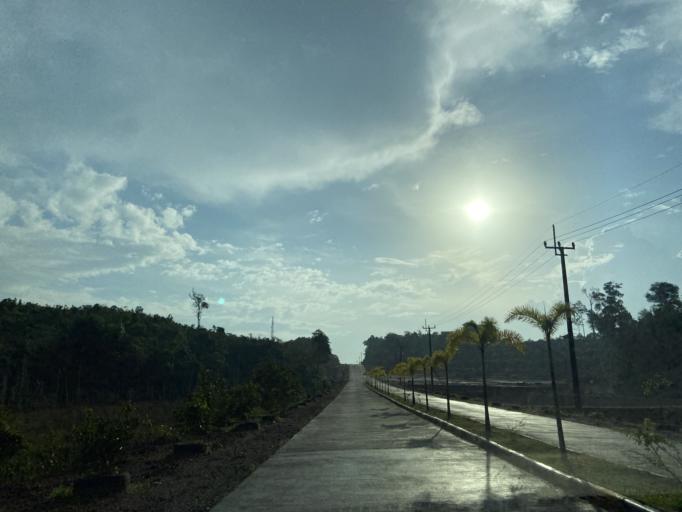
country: ID
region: Riau Islands
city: Tanjungpinang
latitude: 0.8956
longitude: 104.1250
